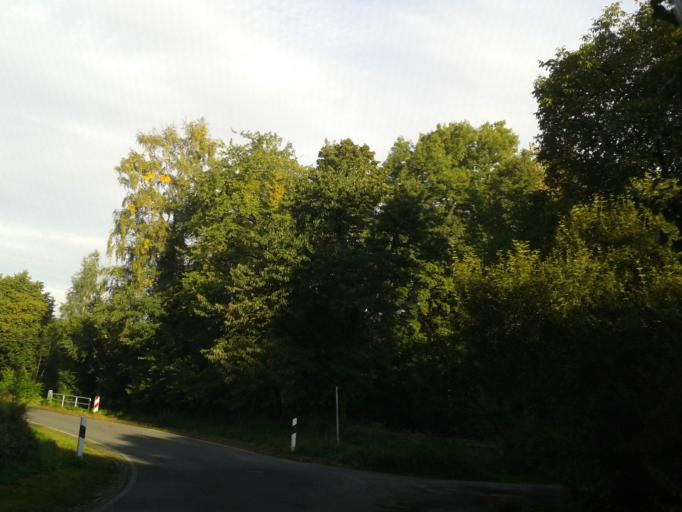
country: DE
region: North Rhine-Westphalia
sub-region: Regierungsbezirk Detmold
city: Barntrup
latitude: 51.9941
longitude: 9.0674
